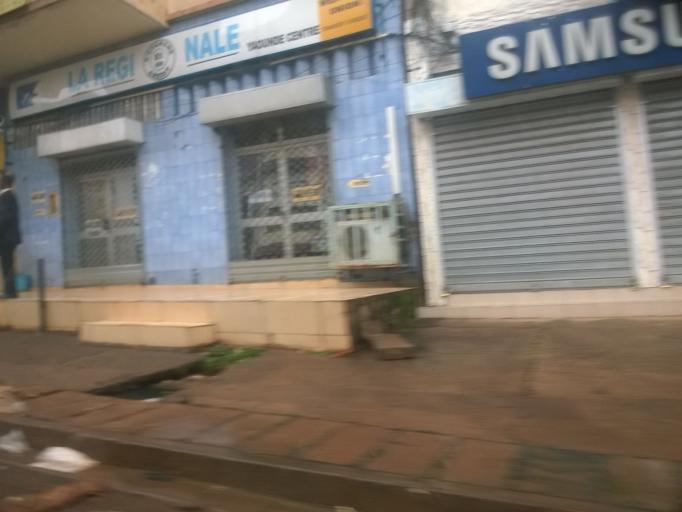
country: CM
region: Centre
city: Yaounde
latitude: 3.8680
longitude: 11.5190
